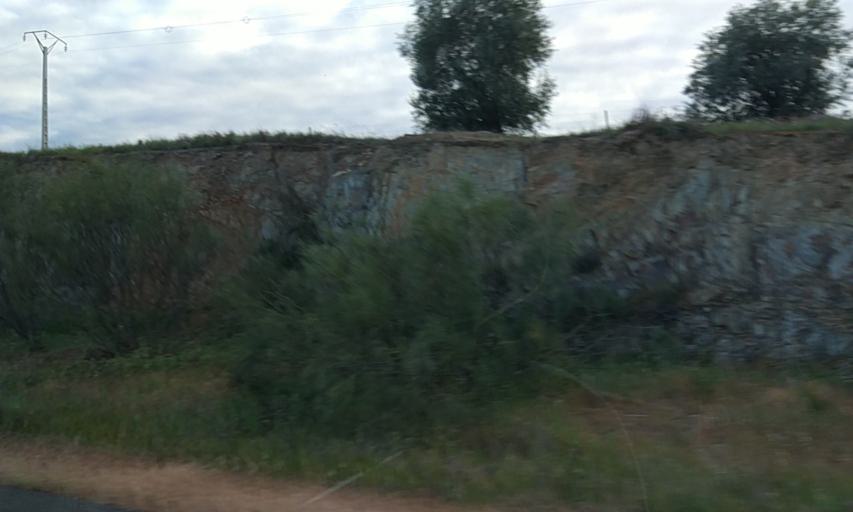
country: ES
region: Extremadura
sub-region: Provincia de Caceres
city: Casar de Caceres
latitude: 39.5846
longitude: -6.4068
